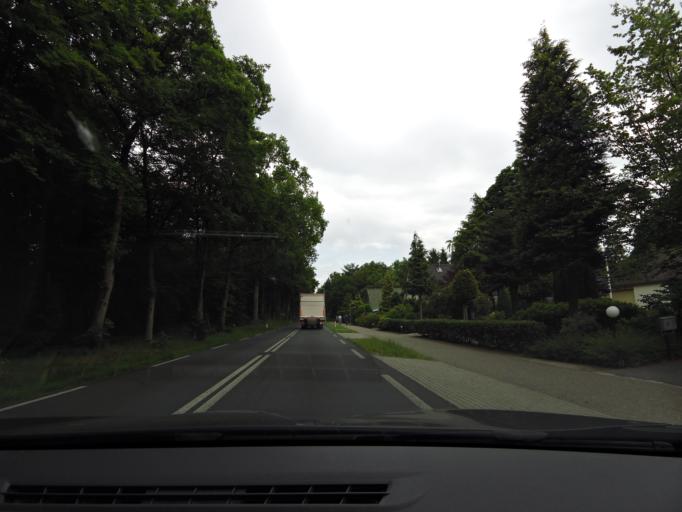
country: NL
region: Gelderland
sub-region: Gemeente Brummen
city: Eerbeek
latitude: 52.1015
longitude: 6.0445
